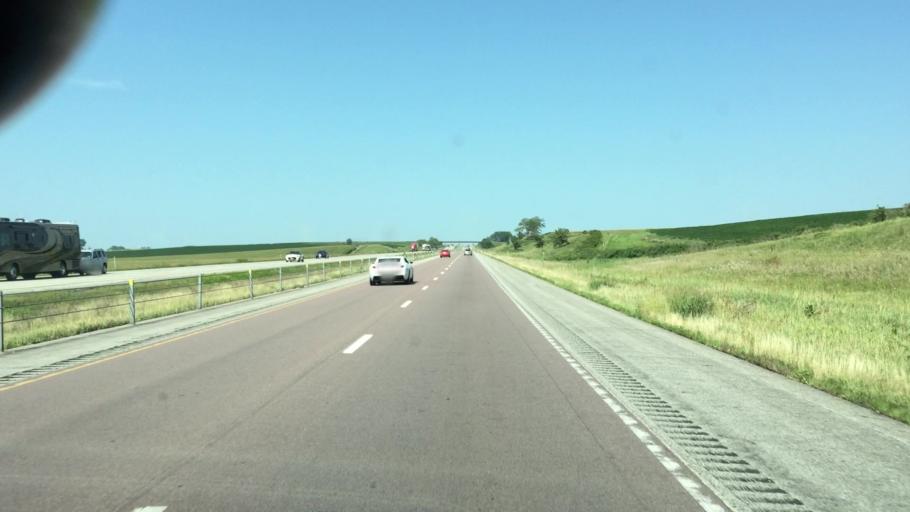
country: US
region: Iowa
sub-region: Iowa County
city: Williamsburg
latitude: 41.6927
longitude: -92.1085
